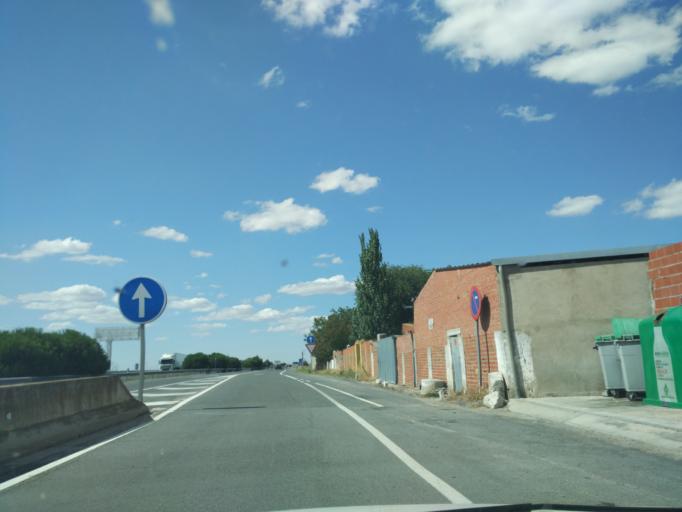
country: ES
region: Castille and Leon
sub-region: Provincia de Valladolid
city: Ataquines
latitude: 41.1823
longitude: -4.8079
